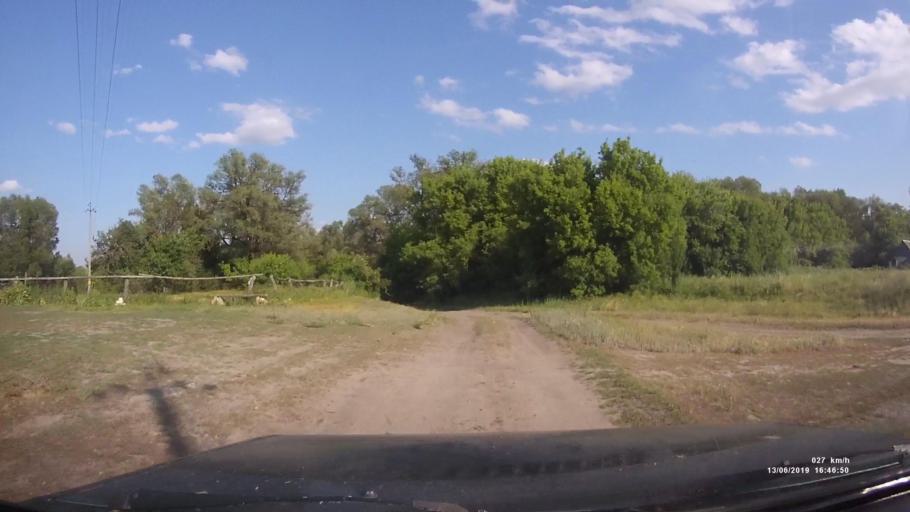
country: RU
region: Rostov
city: Kazanskaya
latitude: 49.9445
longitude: 41.4293
